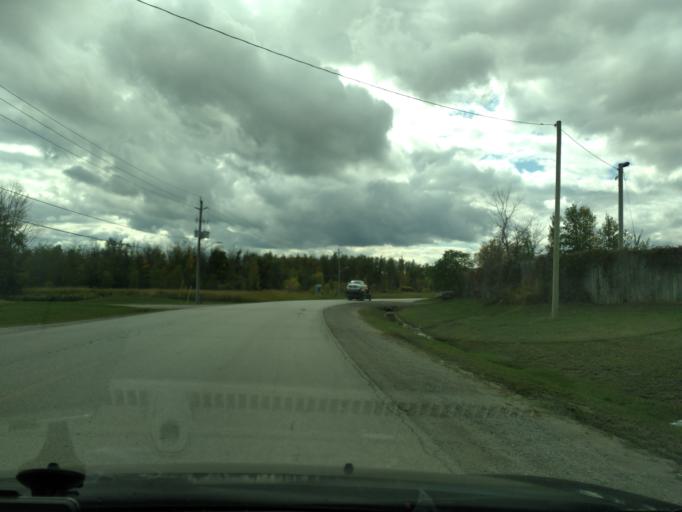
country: CA
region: Ontario
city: Bradford West Gwillimbury
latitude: 44.1328
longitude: -79.5554
